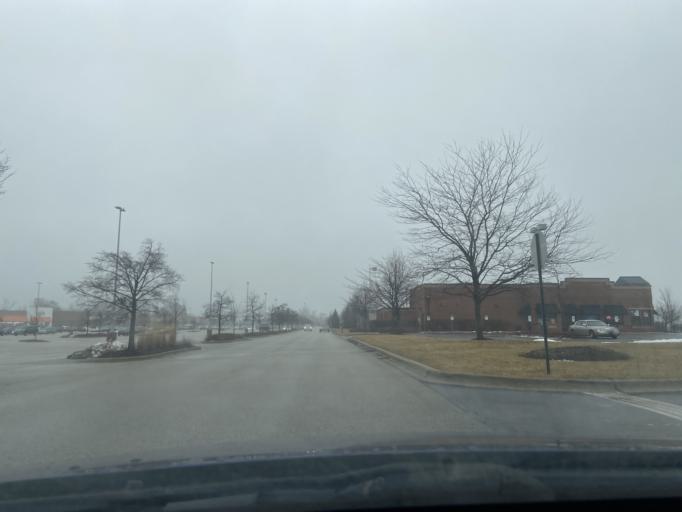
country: US
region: Illinois
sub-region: Lake County
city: Mundelein
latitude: 42.2839
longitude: -88.0466
